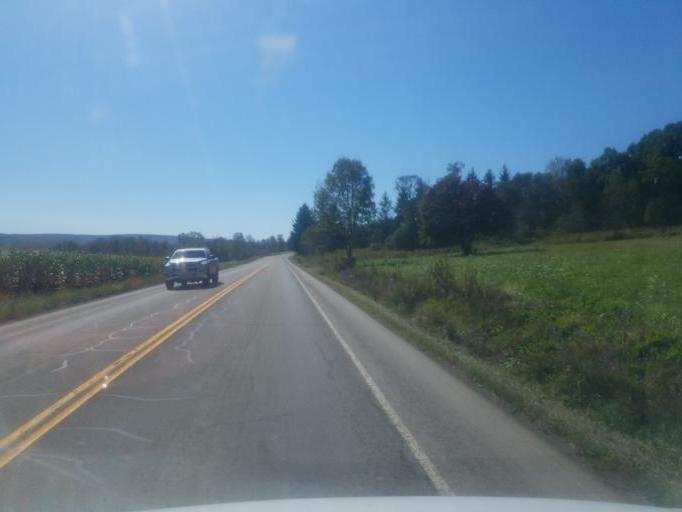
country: US
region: New York
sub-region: Allegany County
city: Friendship
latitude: 42.2982
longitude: -78.1905
